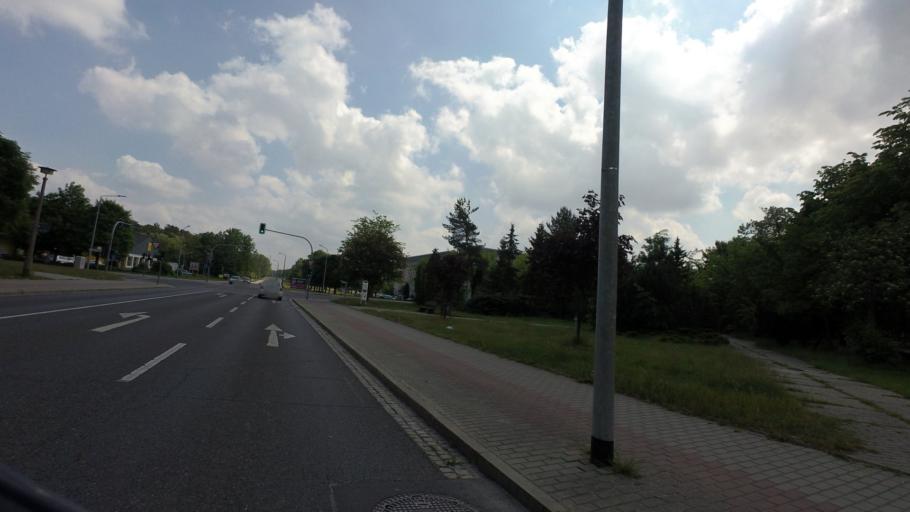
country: DE
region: Saxony
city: Weisswasser
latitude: 51.4969
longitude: 14.6313
